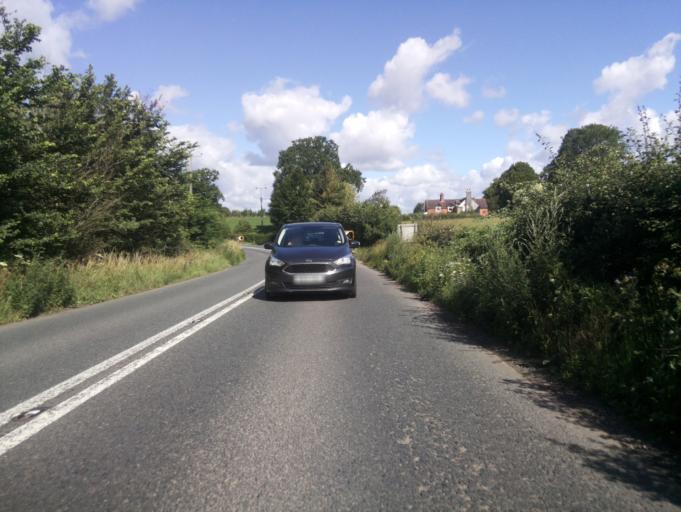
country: GB
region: England
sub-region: Gloucestershire
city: Gloucester
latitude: 51.8895
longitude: -2.3199
